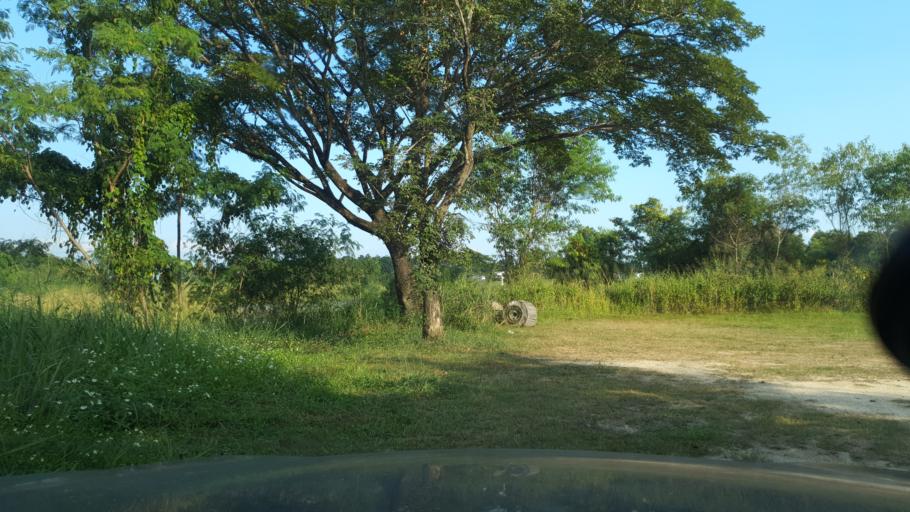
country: TH
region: Chiang Mai
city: Chiang Mai
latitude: 18.8285
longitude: 98.9529
